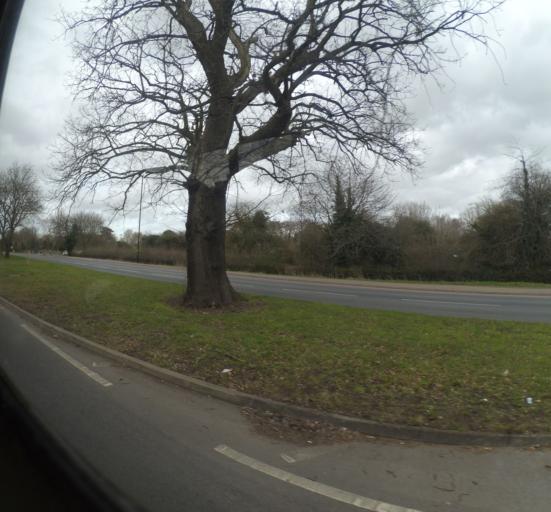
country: GB
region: England
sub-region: Warwickshire
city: Ryton on Dunsmore
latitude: 52.4199
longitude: -1.4468
